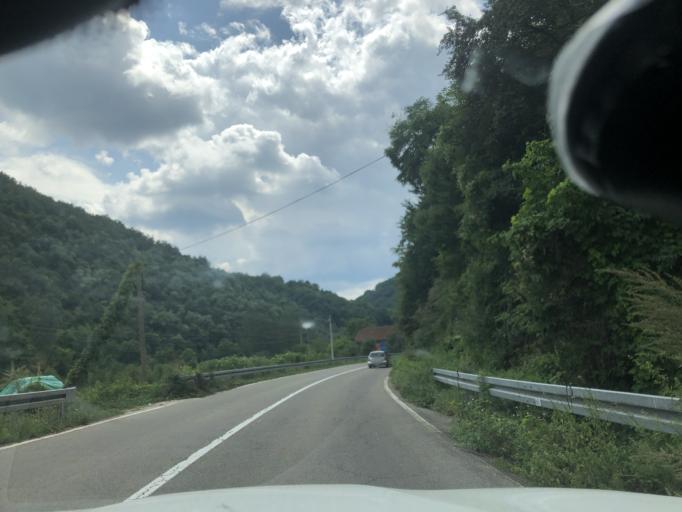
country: RS
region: Central Serbia
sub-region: Jablanicki Okrug
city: Medvega
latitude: 42.8063
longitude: 21.5782
